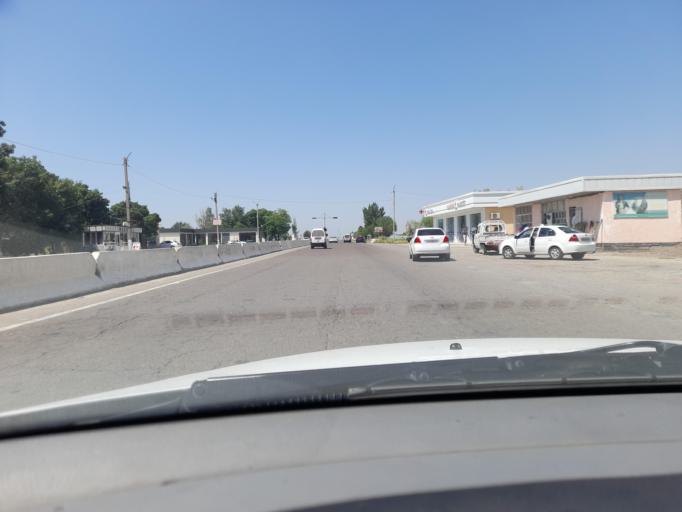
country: UZ
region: Sirdaryo
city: Guliston
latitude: 40.4892
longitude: 68.7391
